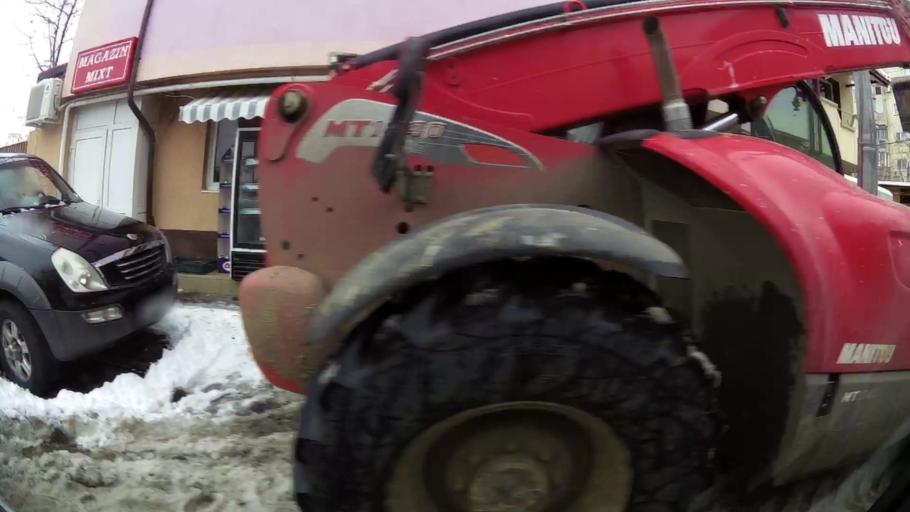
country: RO
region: Bucuresti
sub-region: Municipiul Bucuresti
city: Bucuresti
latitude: 44.3904
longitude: 26.1084
